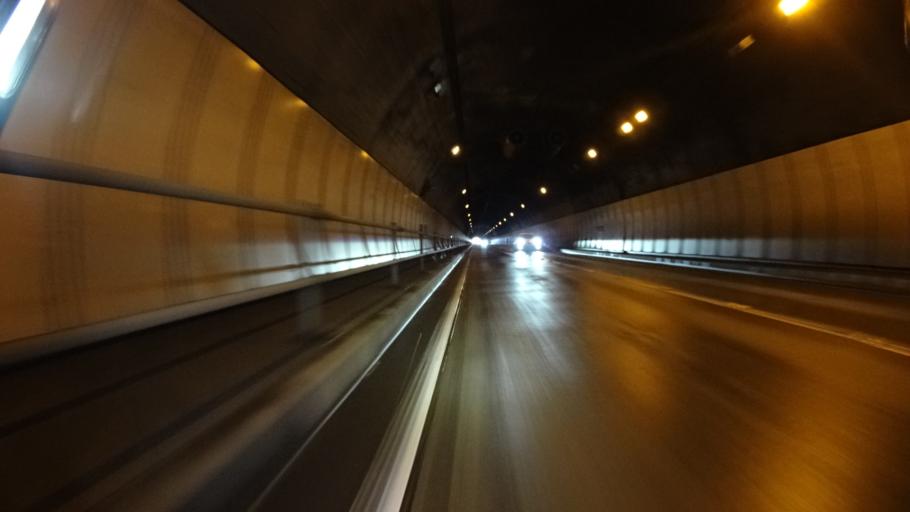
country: JP
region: Tokyo
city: Ome
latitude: 35.8149
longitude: 139.2504
